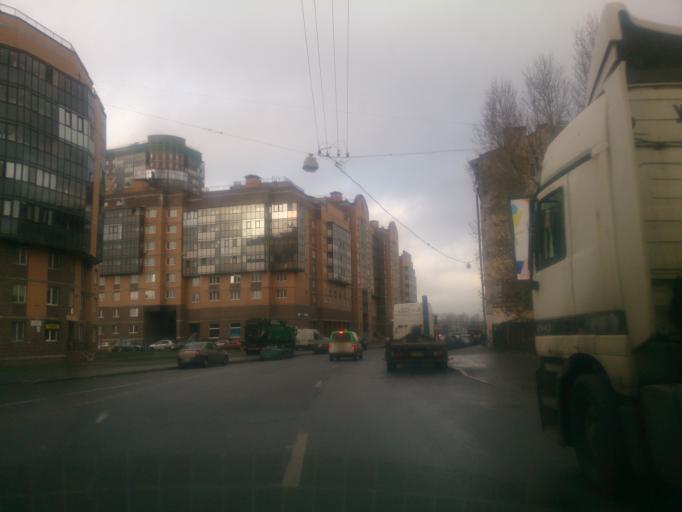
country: RU
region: St.-Petersburg
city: Admiralteisky
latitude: 59.9038
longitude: 30.2908
